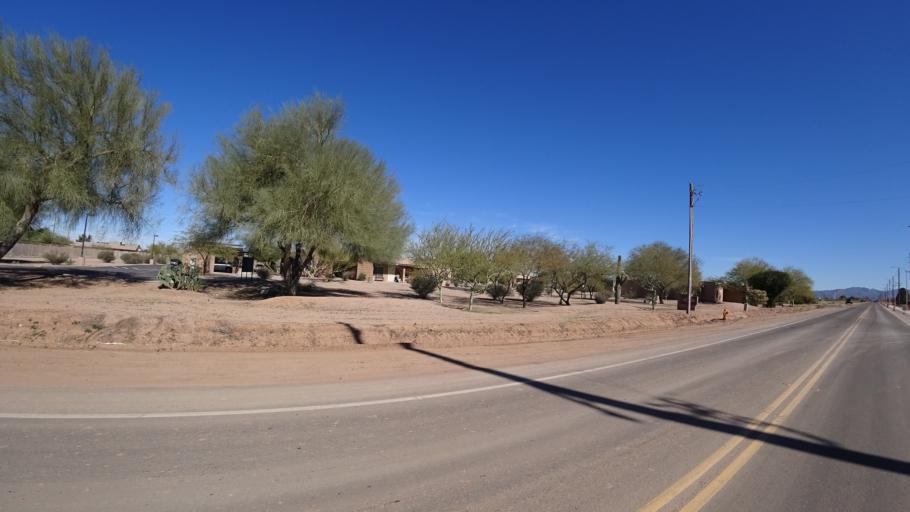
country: US
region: Arizona
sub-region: Maricopa County
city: Scottsdale
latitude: 33.4952
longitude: -111.8278
